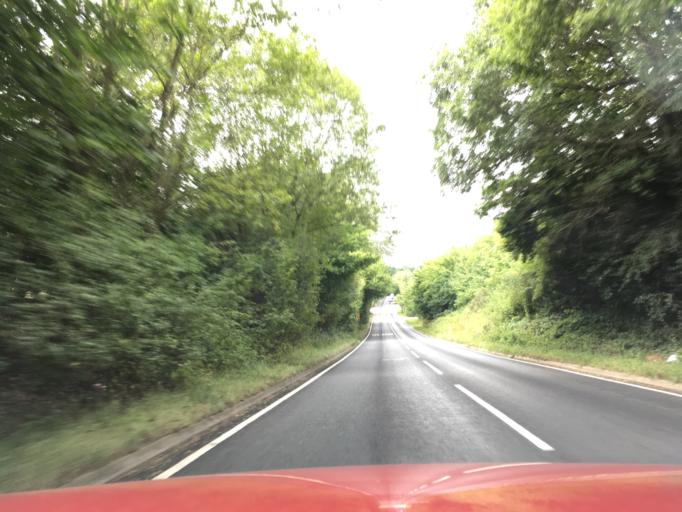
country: GB
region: England
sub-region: Kent
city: Cranbrook
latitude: 51.1114
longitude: 0.5366
